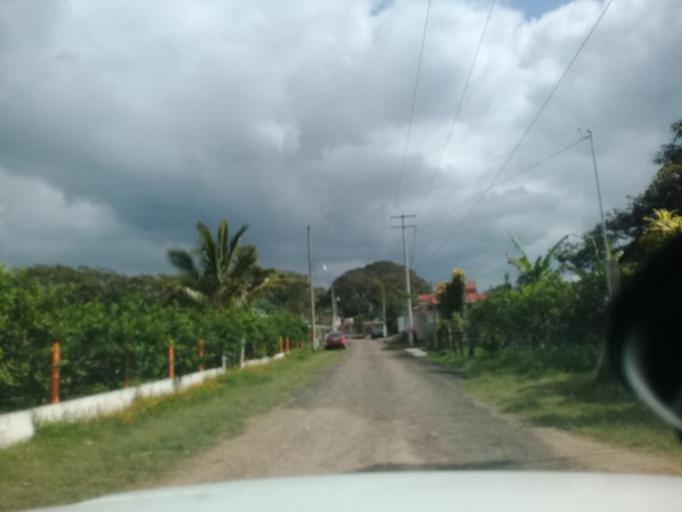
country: MX
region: Veracruz
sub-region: Xalapa
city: Fraccionamiento las Fuentes
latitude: 19.4738
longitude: -96.8776
